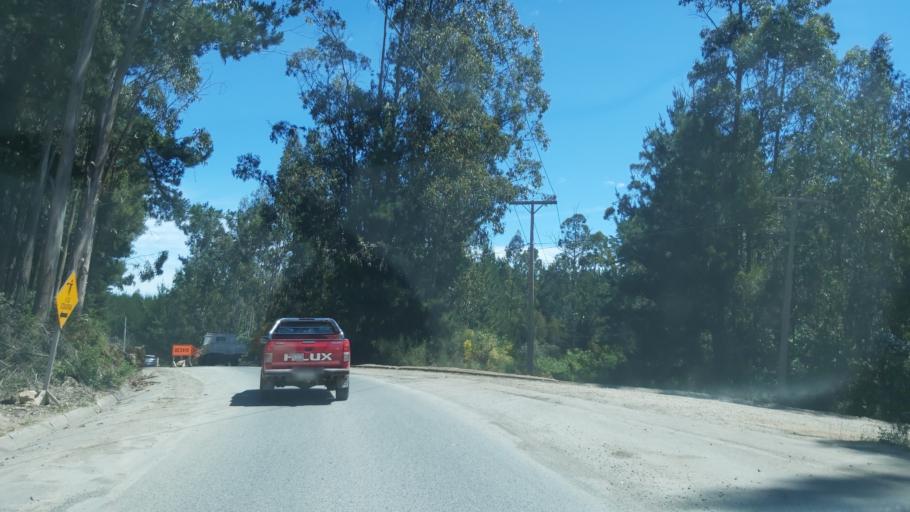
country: CL
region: Maule
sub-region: Provincia de Talca
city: Constitucion
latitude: -35.3760
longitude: -72.4214
